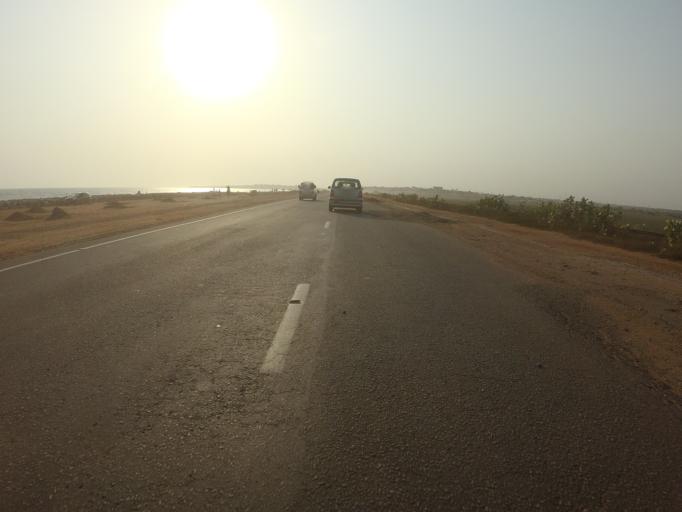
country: GH
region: Greater Accra
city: Nungua
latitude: 5.6133
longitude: -0.0359
